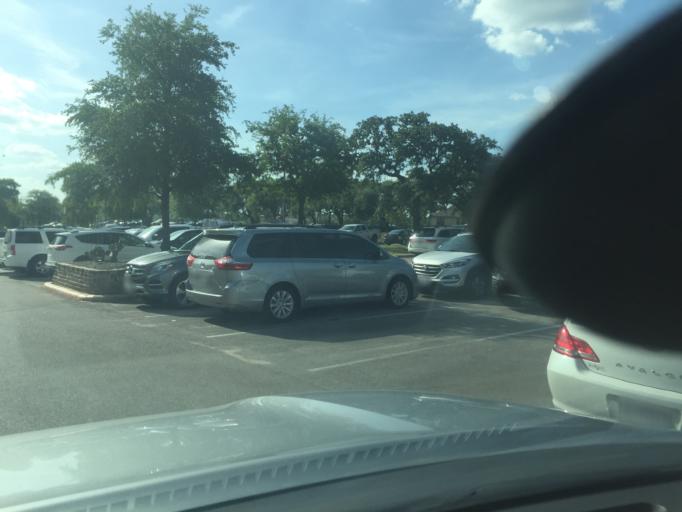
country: US
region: Texas
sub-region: Bexar County
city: Hollywood Park
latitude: 29.6206
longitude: -98.4894
